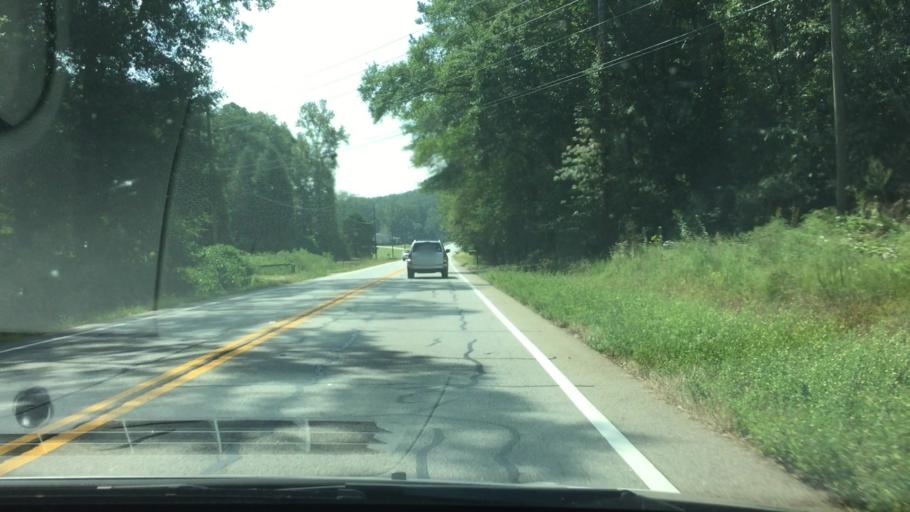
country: US
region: Georgia
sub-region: Henry County
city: McDonough
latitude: 33.5388
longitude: -84.1389
